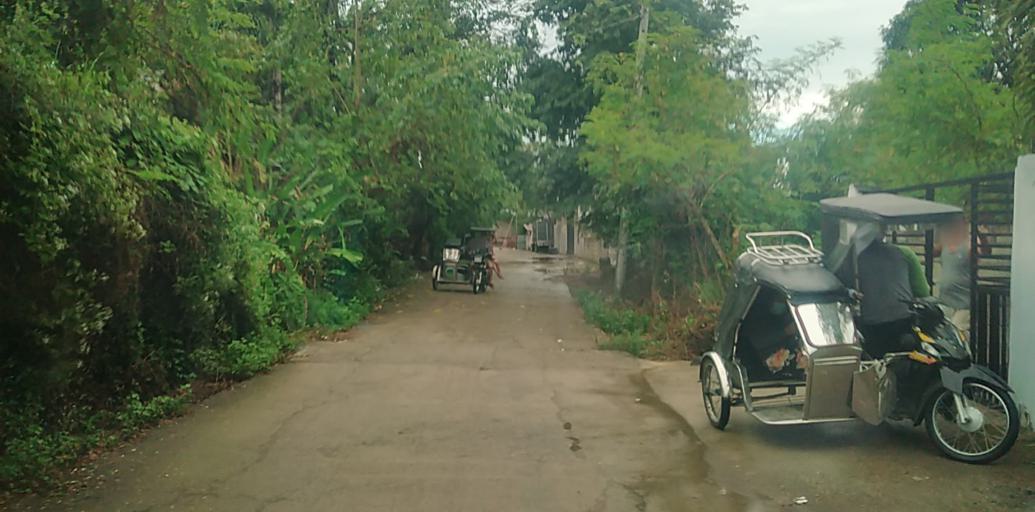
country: PH
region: Central Luzon
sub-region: Province of Pampanga
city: Arayat
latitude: 15.1523
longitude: 120.7452
